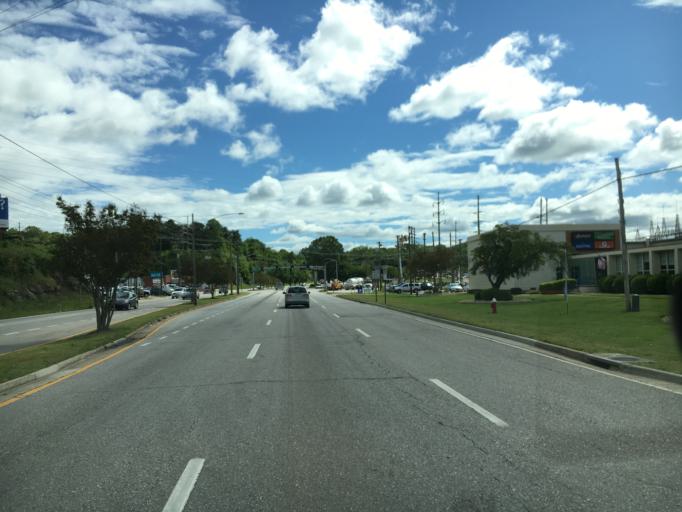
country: US
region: Virginia
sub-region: City of Danville
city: Danville
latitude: 36.5966
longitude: -79.4002
